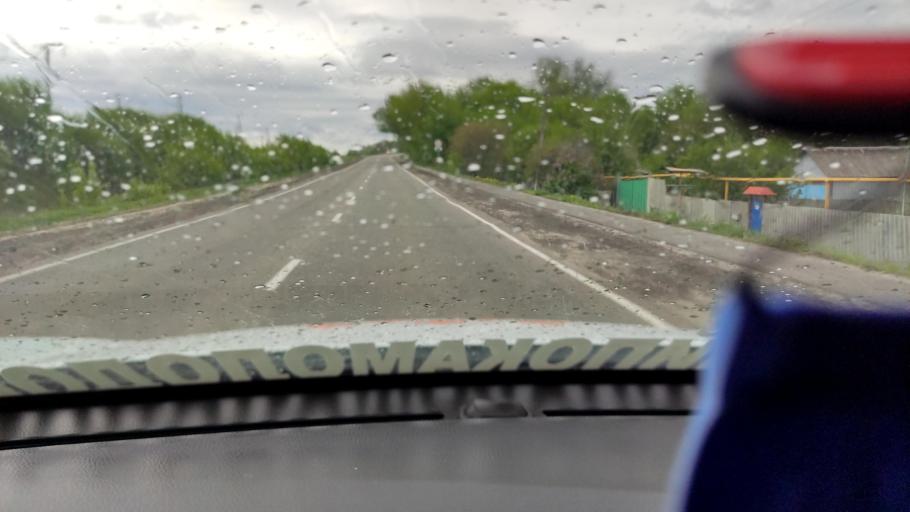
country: RU
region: Voronezj
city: Imeni Pervogo Maya
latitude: 50.7542
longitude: 39.3884
